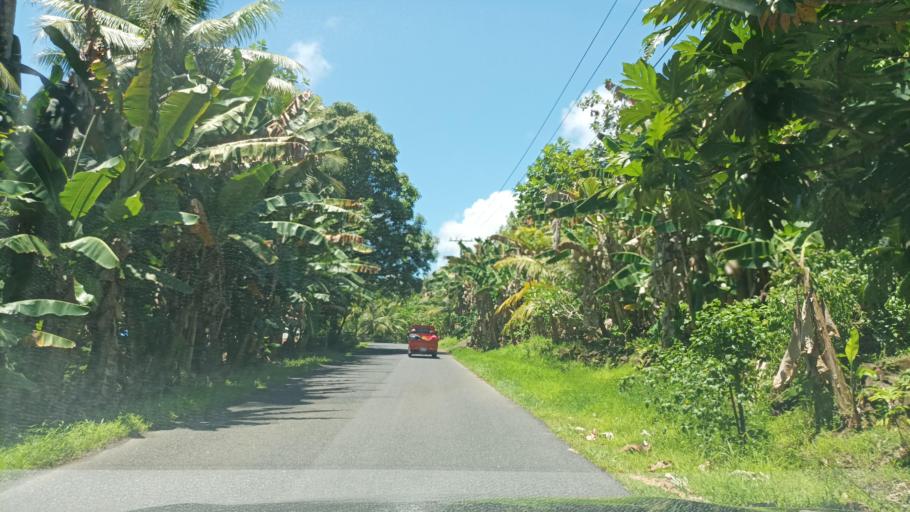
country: FM
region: Pohnpei
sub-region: Kolonia Municipality
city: Kolonia
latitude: 6.9589
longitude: 158.2784
